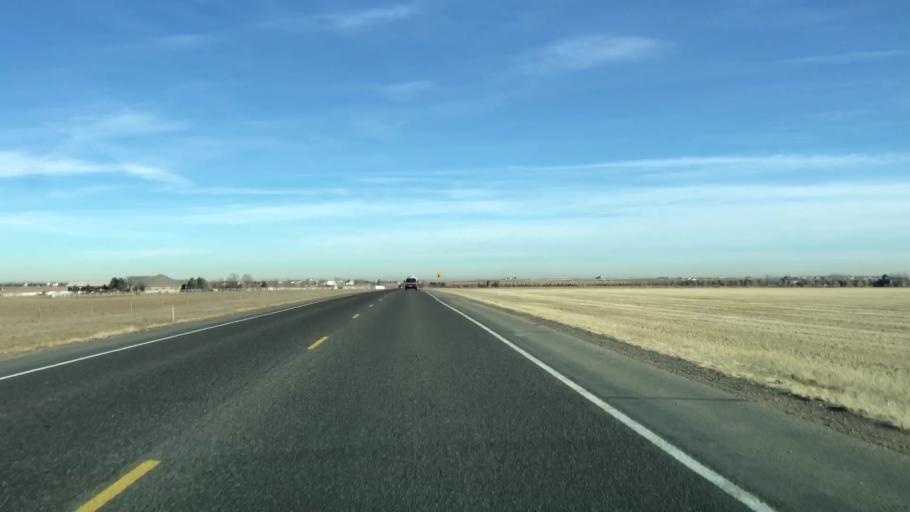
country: US
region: Colorado
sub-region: Weld County
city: Windsor
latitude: 40.4187
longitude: -104.9443
